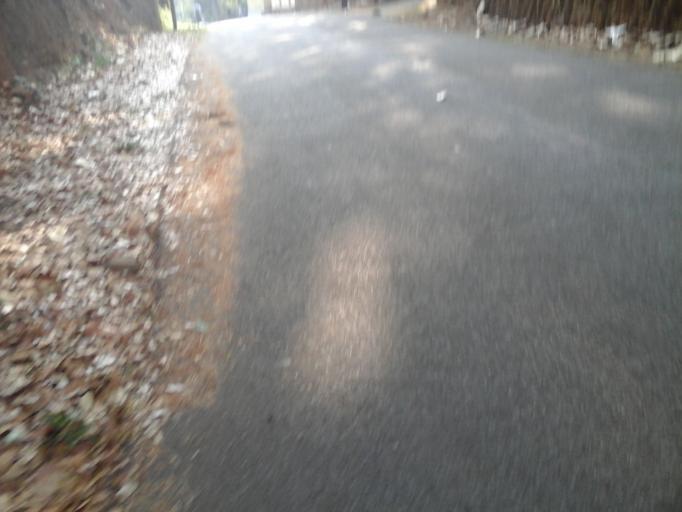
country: IN
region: Kerala
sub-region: Kottayam
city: Erattupetta
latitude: 9.5941
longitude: 76.7296
